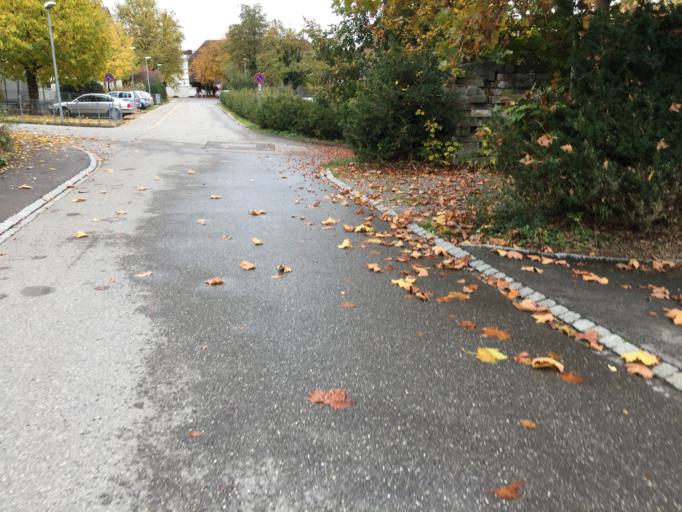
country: CH
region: Bern
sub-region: Bern-Mittelland District
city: Munsingen
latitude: 46.8773
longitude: 7.5603
